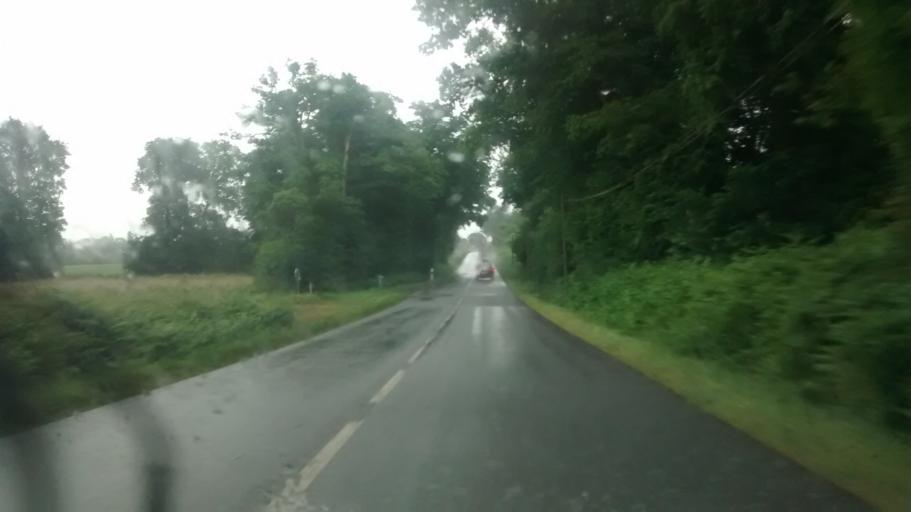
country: FR
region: Brittany
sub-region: Departement du Morbihan
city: La Gacilly
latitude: 47.7789
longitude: -2.1641
